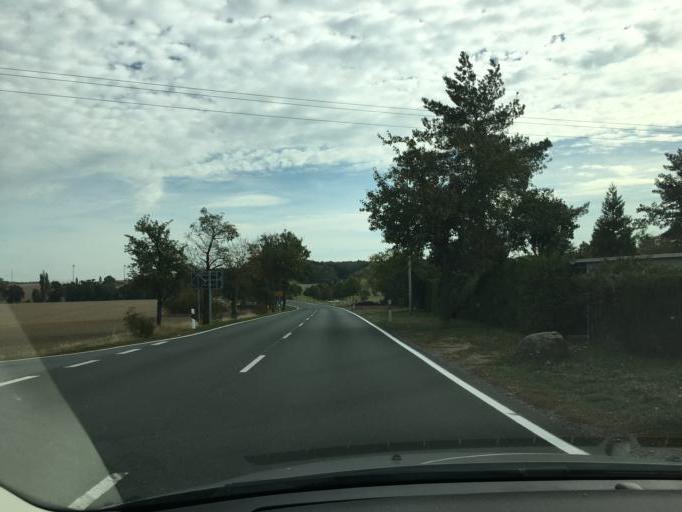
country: DE
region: Saxony
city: Oschatz
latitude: 51.2877
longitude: 13.1457
